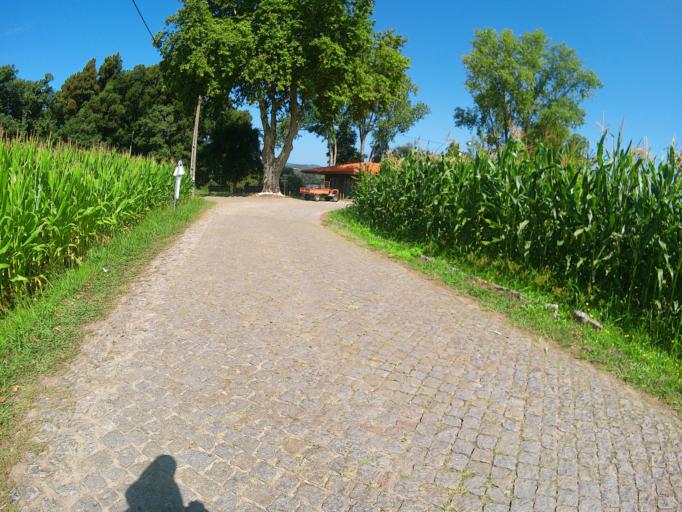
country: ES
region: Galicia
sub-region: Provincia de Pontevedra
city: O Rosal
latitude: 41.9103
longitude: -8.7932
